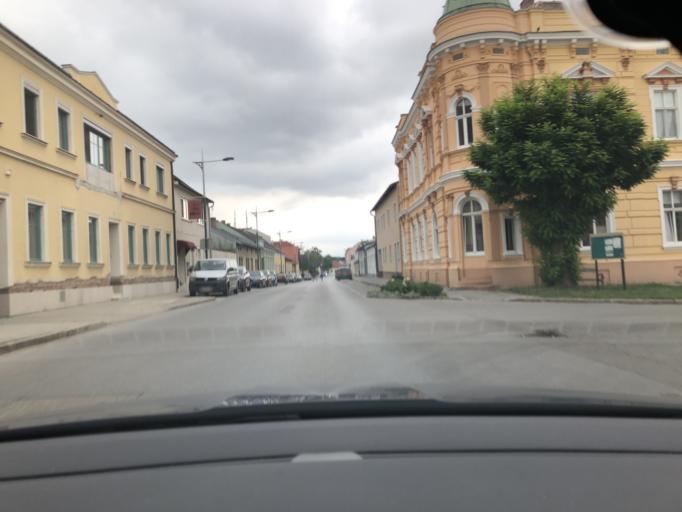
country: AT
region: Lower Austria
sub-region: Politischer Bezirk Mistelbach
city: Laa an der Thaya
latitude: 48.7234
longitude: 16.3845
